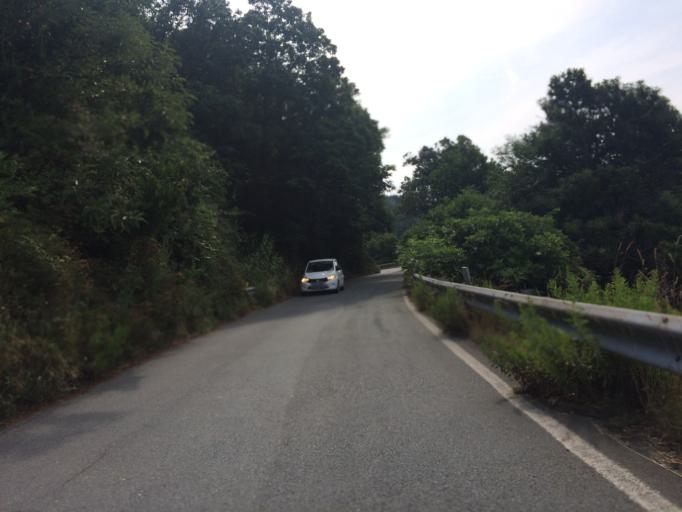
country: IT
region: Liguria
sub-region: Provincia di Savona
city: San Giovanni
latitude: 44.3958
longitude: 8.5015
